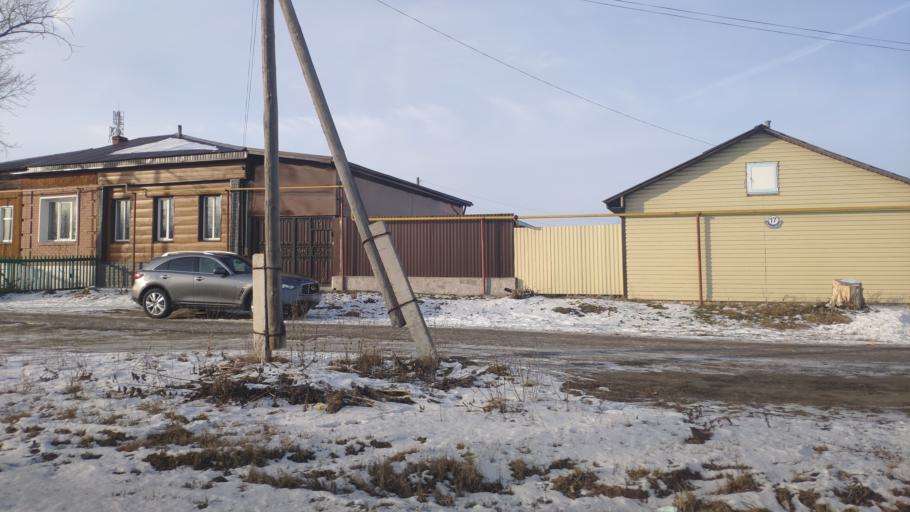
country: RU
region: Kurgan
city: Shadrinsk
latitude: 56.0886
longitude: 63.6744
